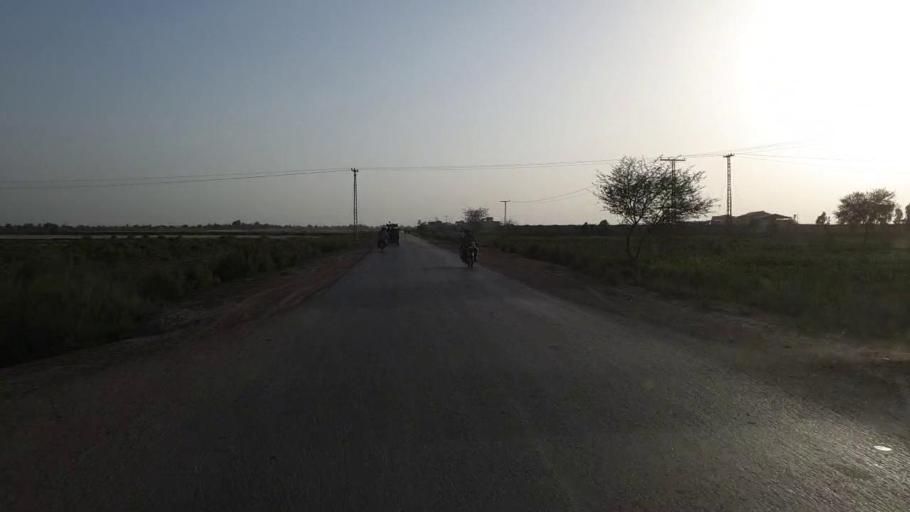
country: PK
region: Sindh
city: Jam Sahib
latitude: 26.2908
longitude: 68.6114
